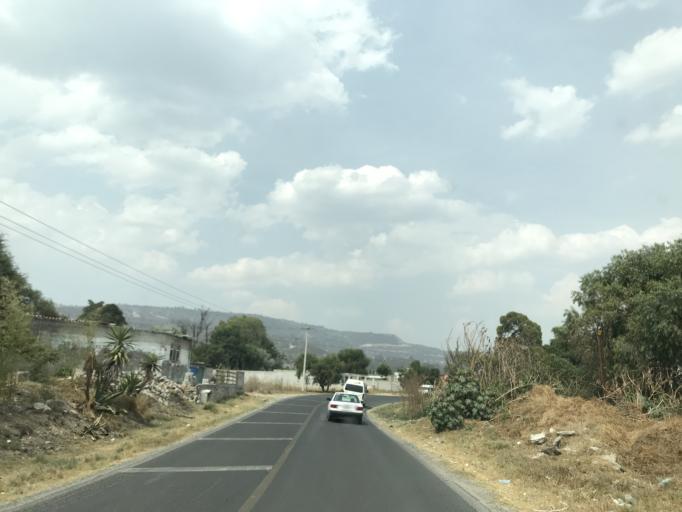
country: MX
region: Tlaxcala
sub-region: Panotla
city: Fraccionamiento la Virgen
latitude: 19.3203
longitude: -98.3041
